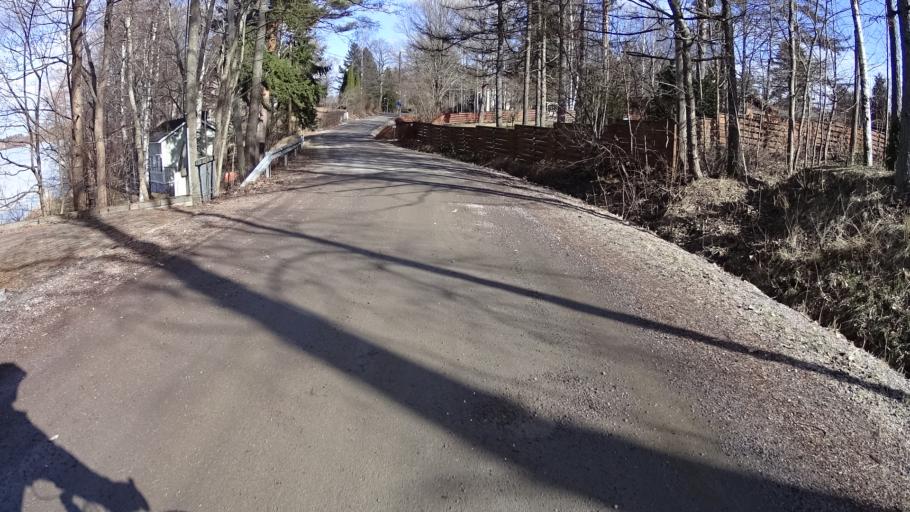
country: FI
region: Uusimaa
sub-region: Helsinki
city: Kilo
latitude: 60.2509
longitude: 24.7550
